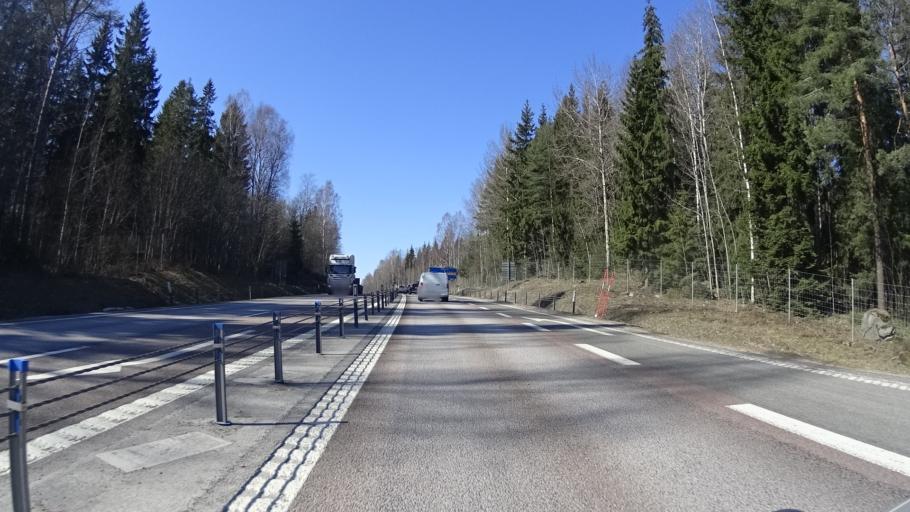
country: SE
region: Vaermland
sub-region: Kristinehamns Kommun
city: Kristinehamn
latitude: 59.3518
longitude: 14.0772
